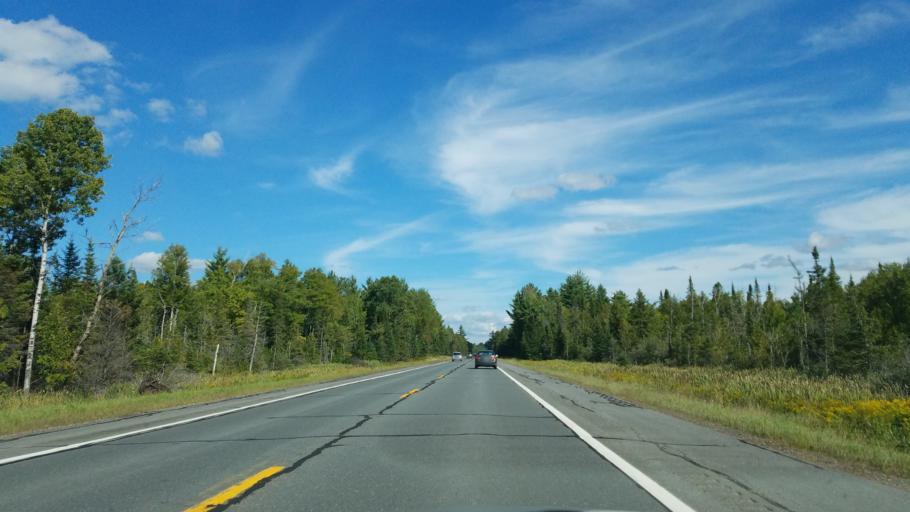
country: US
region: Michigan
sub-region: Baraga County
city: L'Anse
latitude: 46.5789
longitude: -88.3936
